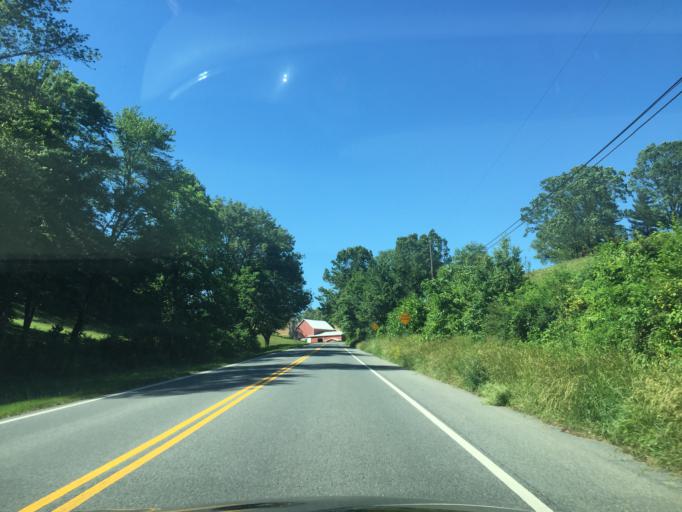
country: US
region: Maryland
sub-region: Carroll County
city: Westminster
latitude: 39.5701
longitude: -76.9423
